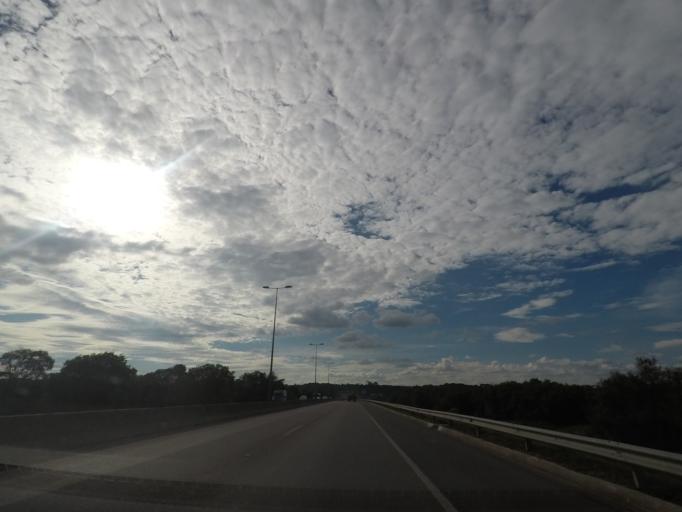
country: BR
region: Parana
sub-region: Araucaria
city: Araucaria
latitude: -25.6195
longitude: -49.3167
